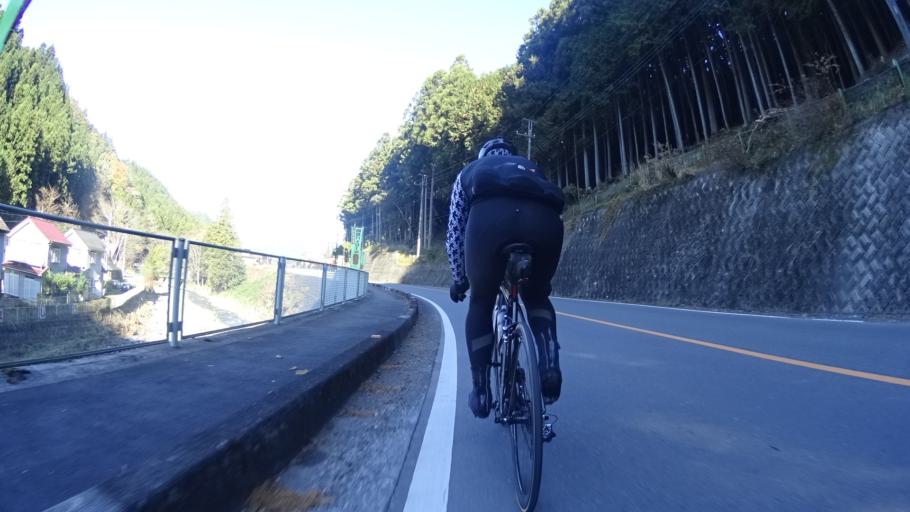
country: JP
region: Tokyo
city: Ome
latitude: 35.8731
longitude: 139.1874
